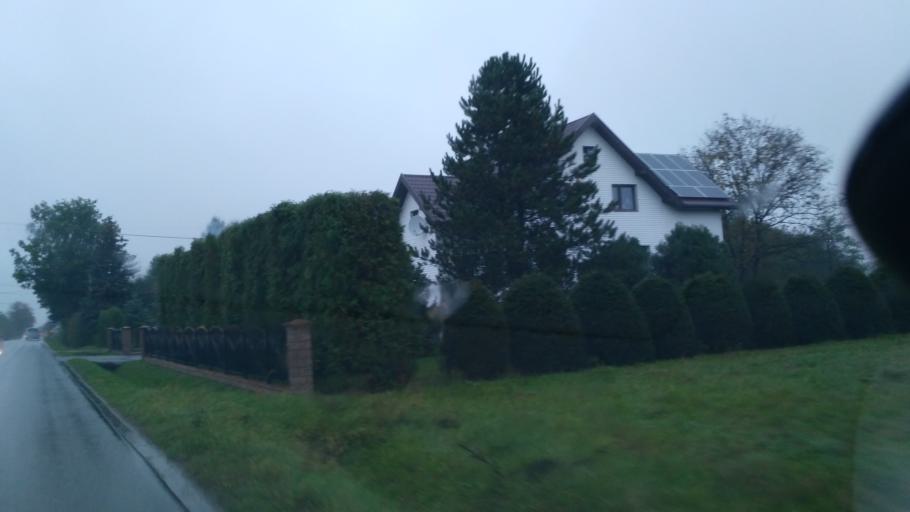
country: PL
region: Subcarpathian Voivodeship
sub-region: Powiat krosnienski
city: Miejsce Piastowe
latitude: 49.6585
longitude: 21.8037
